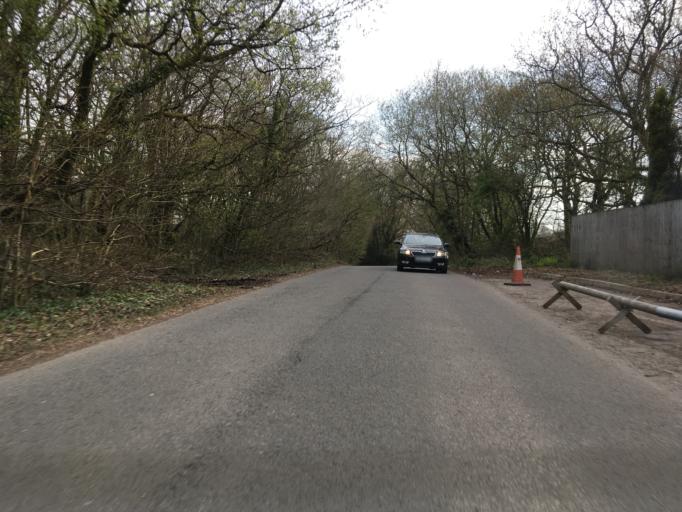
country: GB
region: Wales
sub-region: Caerphilly County Borough
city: Caerphilly
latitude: 51.5538
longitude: -3.2376
